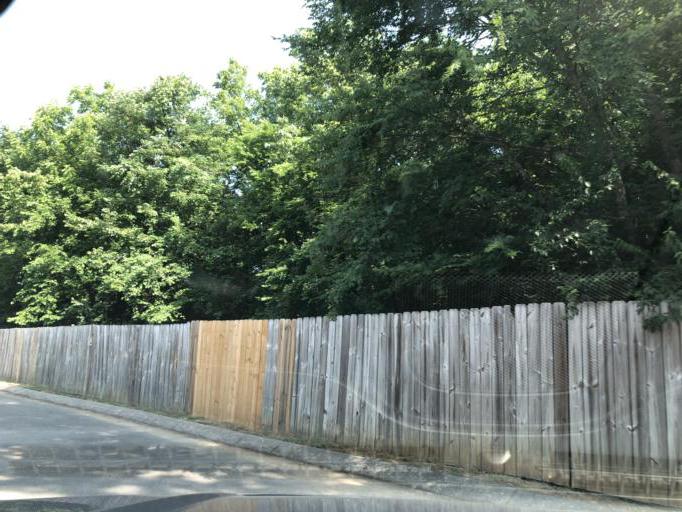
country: US
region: Tennessee
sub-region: Rutherford County
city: La Vergne
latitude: 36.0462
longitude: -86.6384
